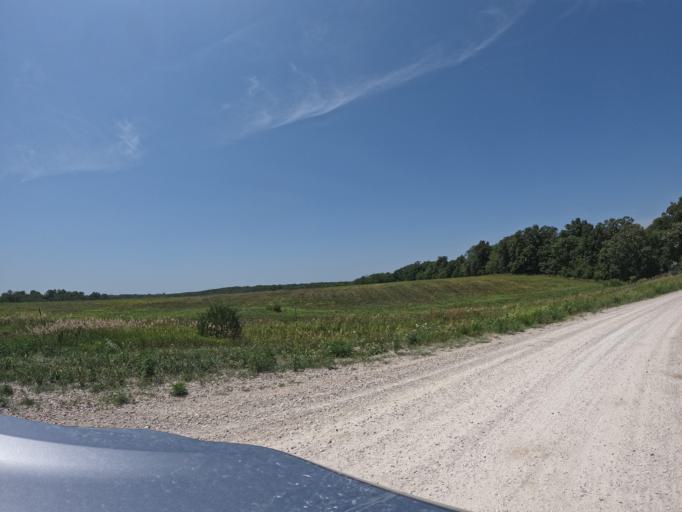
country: US
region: Iowa
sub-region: Henry County
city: Mount Pleasant
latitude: 40.9157
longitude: -91.6652
